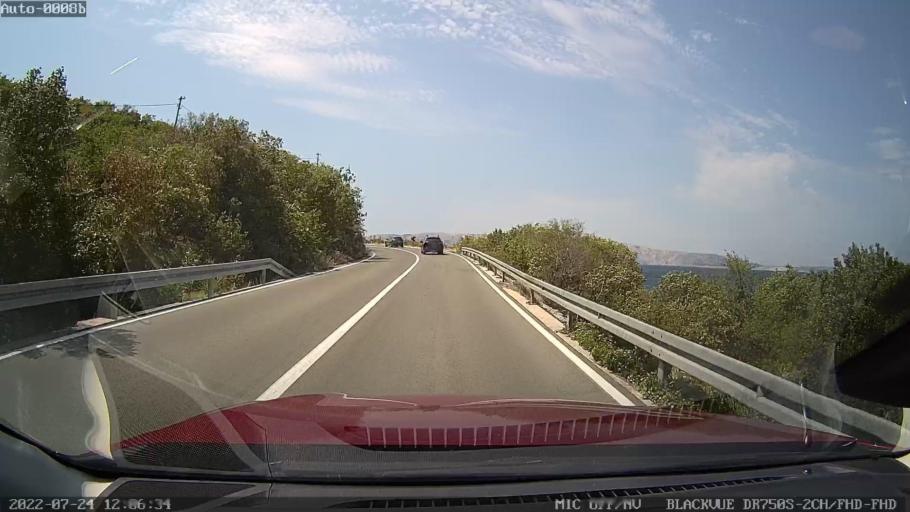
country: HR
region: Licko-Senjska
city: Senj
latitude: 45.0433
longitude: 14.8786
